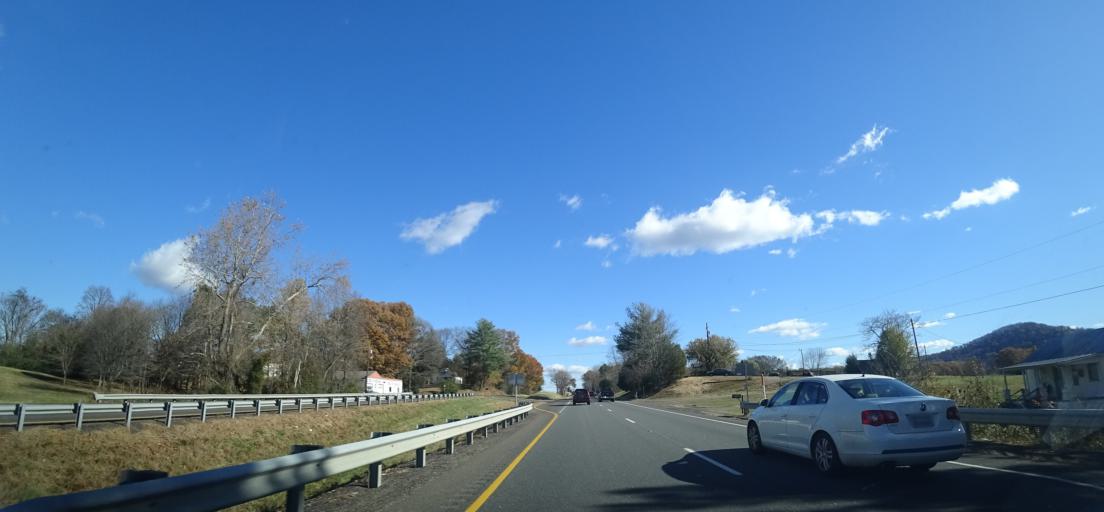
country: US
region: Virginia
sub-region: Madison County
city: Brightwood
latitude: 38.4254
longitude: -78.1807
